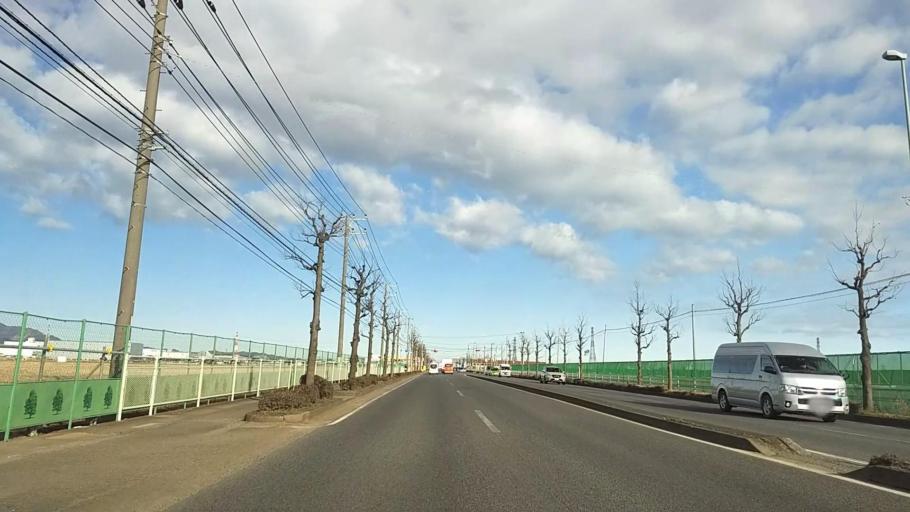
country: JP
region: Kanagawa
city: Atsugi
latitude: 35.3902
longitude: 139.3616
